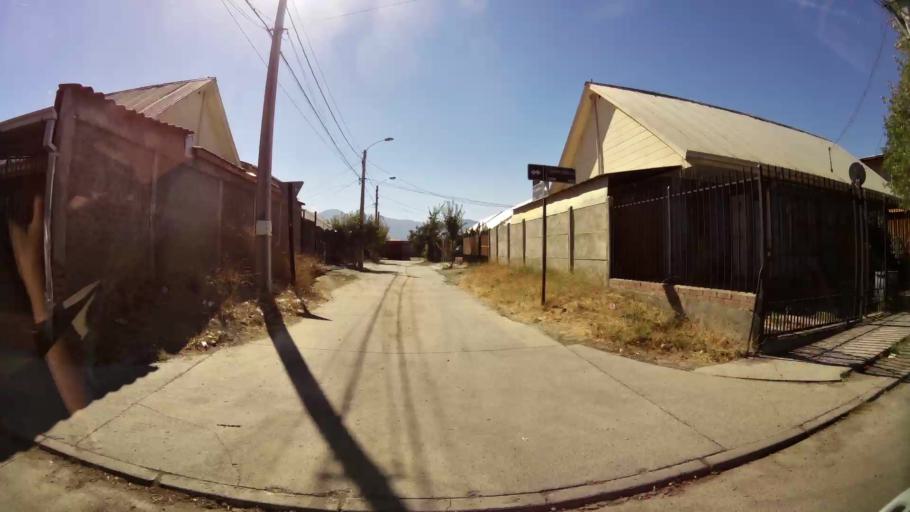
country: CL
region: O'Higgins
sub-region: Provincia de Cachapoal
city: Rancagua
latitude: -34.1813
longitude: -70.7723
